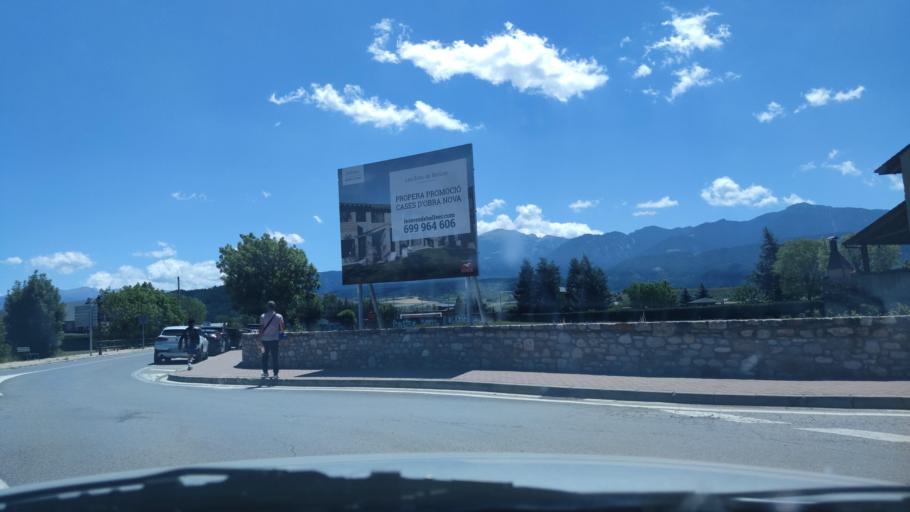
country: ES
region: Catalonia
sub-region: Provincia de Lleida
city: Bellver de Cerdanya
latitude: 42.3697
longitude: 1.7829
